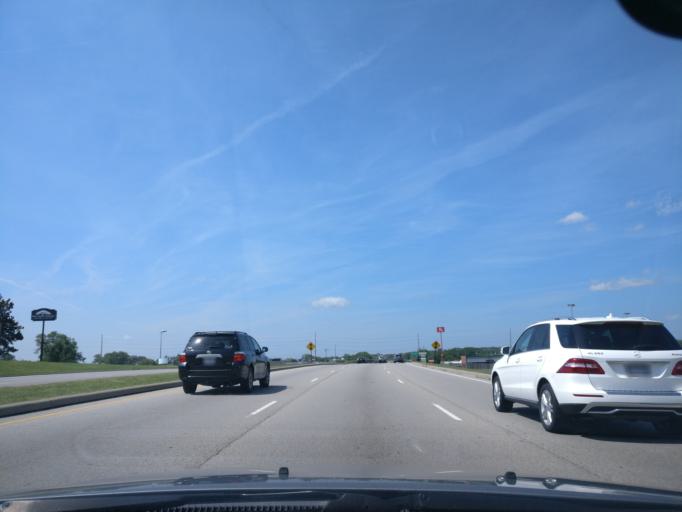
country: US
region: Ohio
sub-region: Butler County
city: Mayfield
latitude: 39.4942
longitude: -84.3324
